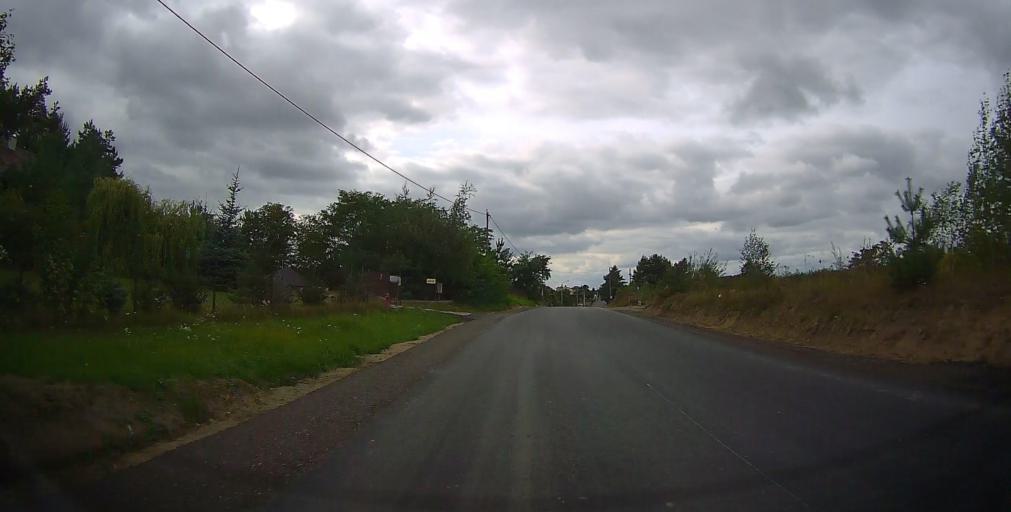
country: PL
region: Masovian Voivodeship
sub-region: Powiat grojecki
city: Belsk Duzy
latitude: 51.8075
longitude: 20.8472
